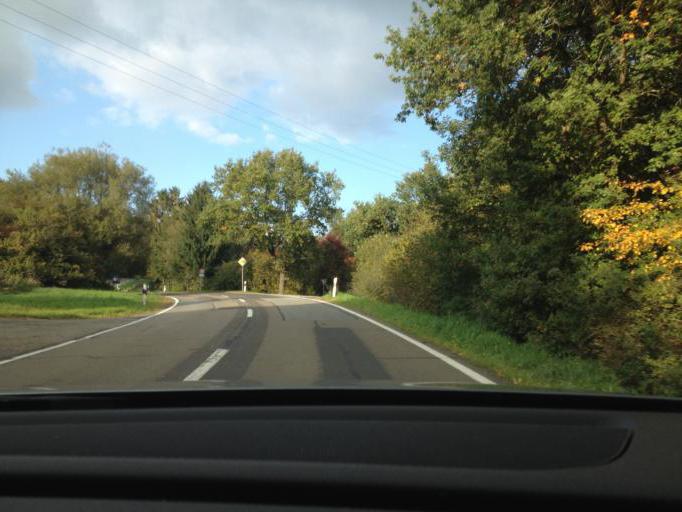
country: DE
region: Saarland
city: Freisen
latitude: 49.5165
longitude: 7.2483
